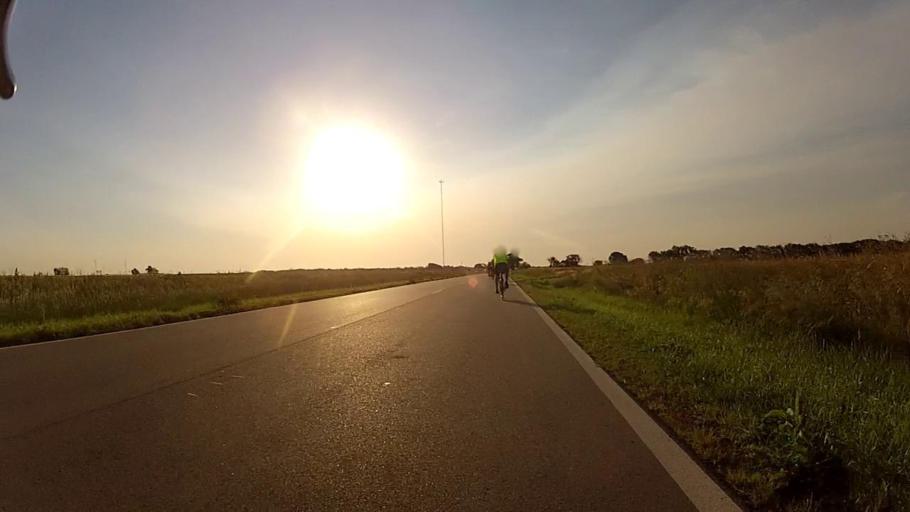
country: US
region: Kansas
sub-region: Harper County
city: Anthony
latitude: 37.1537
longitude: -97.8633
